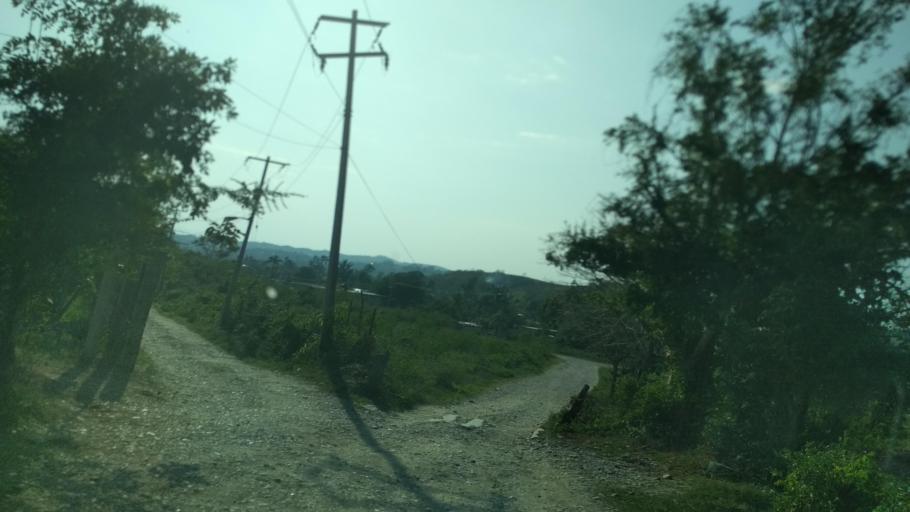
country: MM
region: Shan
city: Taunggyi
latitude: 20.4004
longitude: 97.3311
